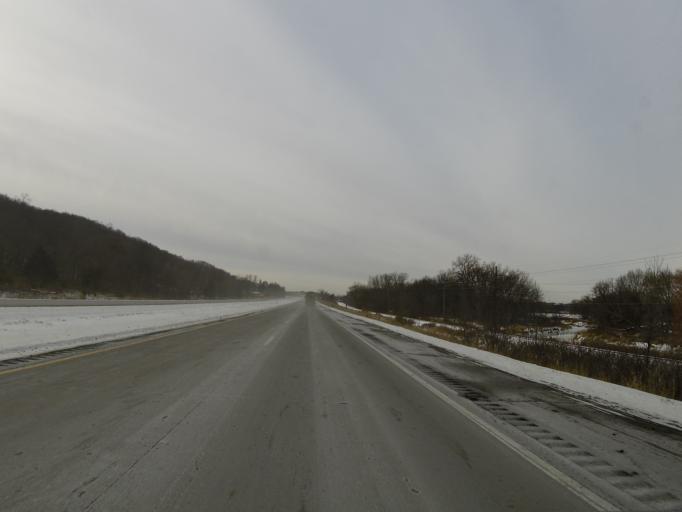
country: US
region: Minnesota
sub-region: Scott County
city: Jordan
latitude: 44.6871
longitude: -93.6113
